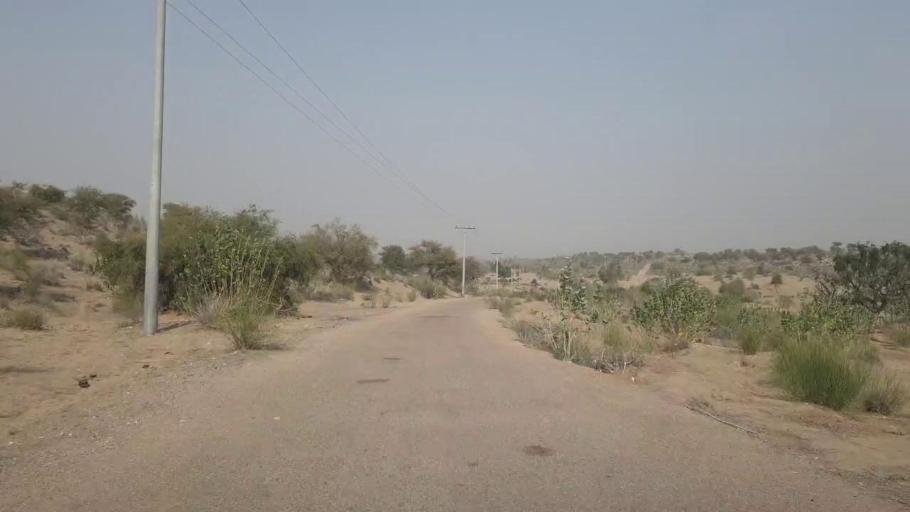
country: PK
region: Sindh
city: Chor
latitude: 25.6295
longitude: 70.0341
